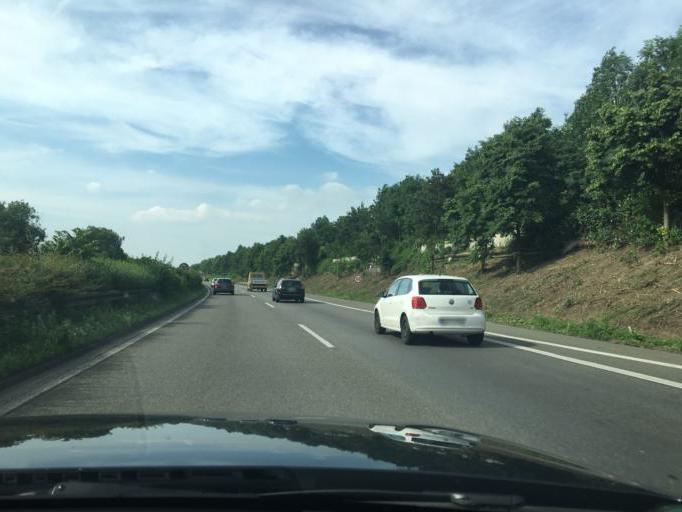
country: DE
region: North Rhine-Westphalia
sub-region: Regierungsbezirk Dusseldorf
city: Hochfeld
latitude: 51.3747
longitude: 6.7756
